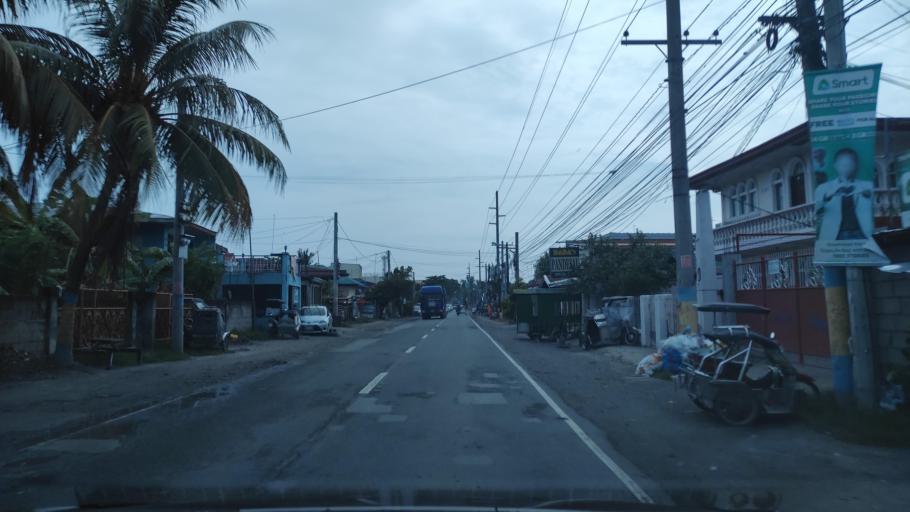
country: PH
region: Central Luzon
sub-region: Province of Pampanga
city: Santa Ana
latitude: 15.1163
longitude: 120.7742
